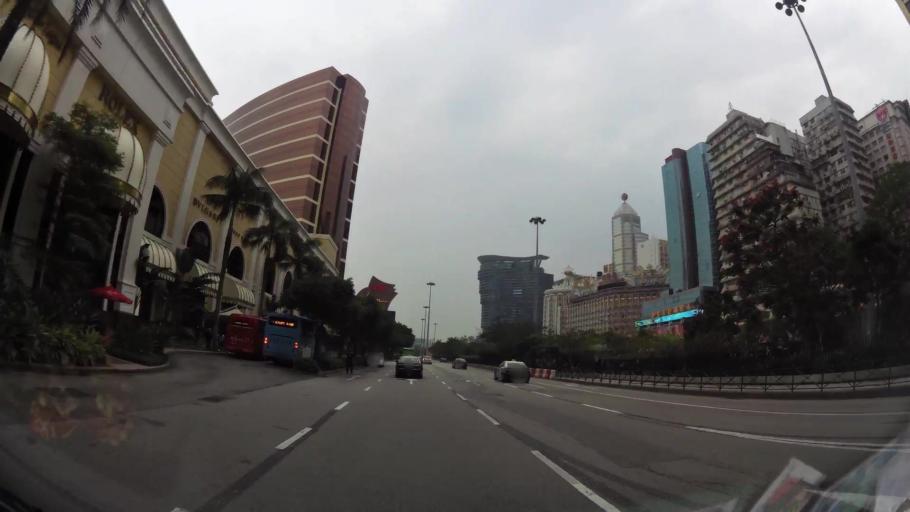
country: MO
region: Macau
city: Macau
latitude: 22.1896
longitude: 113.5473
